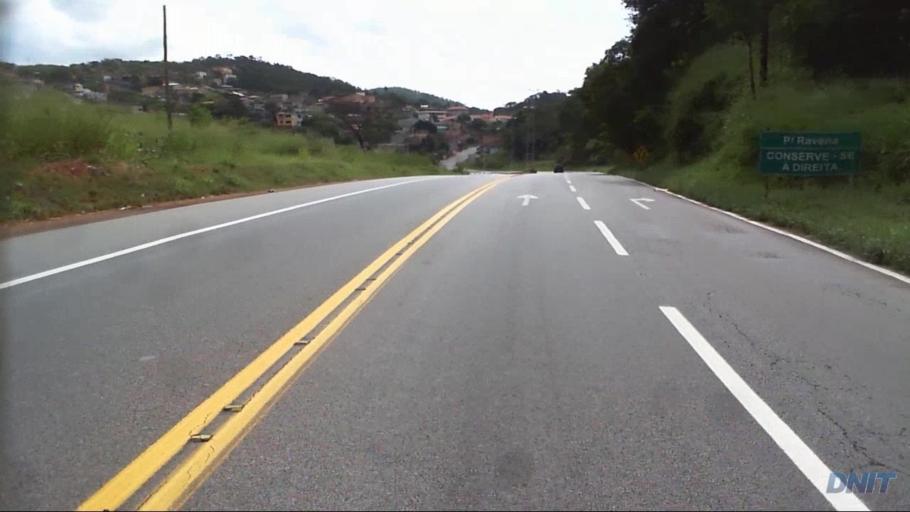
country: BR
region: Minas Gerais
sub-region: Santa Luzia
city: Santa Luzia
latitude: -19.8002
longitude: -43.7527
